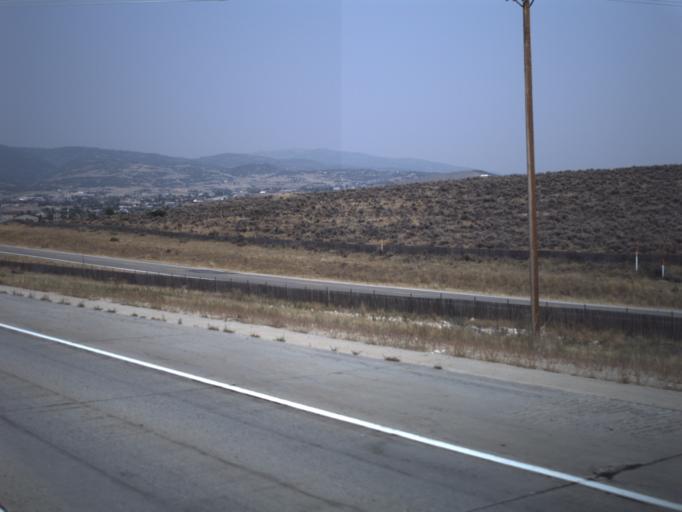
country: US
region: Utah
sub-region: Summit County
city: Snyderville
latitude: 40.7265
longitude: -111.4935
